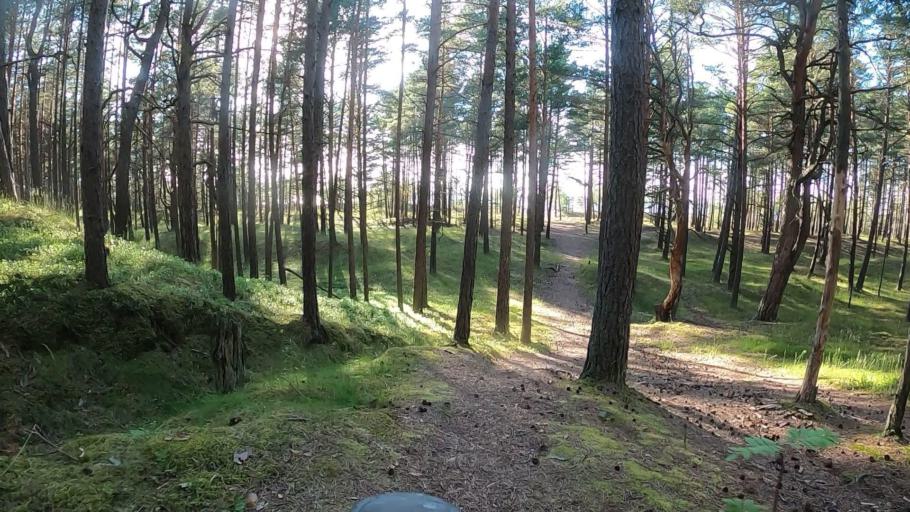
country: LV
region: Carnikava
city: Carnikava
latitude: 57.1263
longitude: 24.2178
